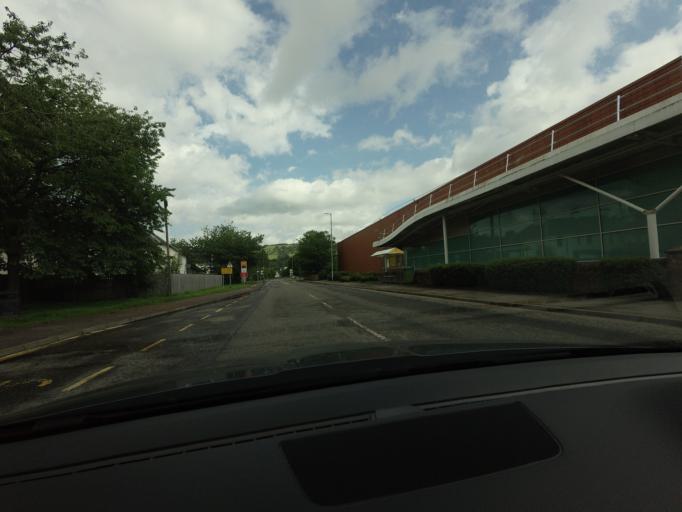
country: GB
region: Scotland
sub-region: Highland
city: Dingwall
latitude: 57.5973
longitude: -4.4316
